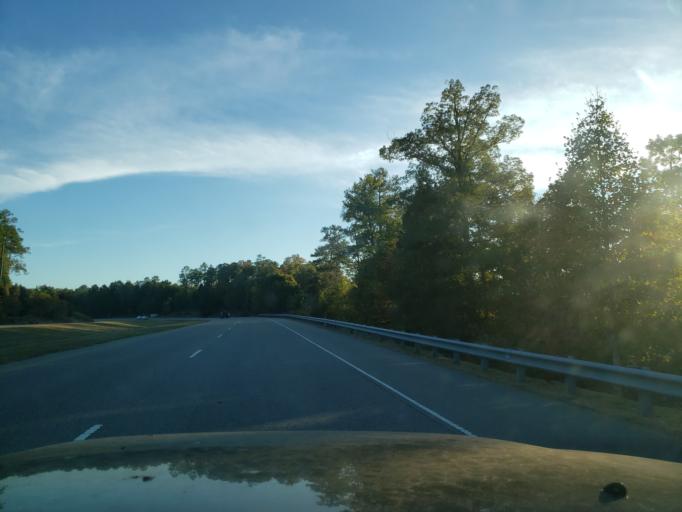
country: US
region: North Carolina
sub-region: Wake County
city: Morrisville
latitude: 35.8640
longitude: -78.8725
